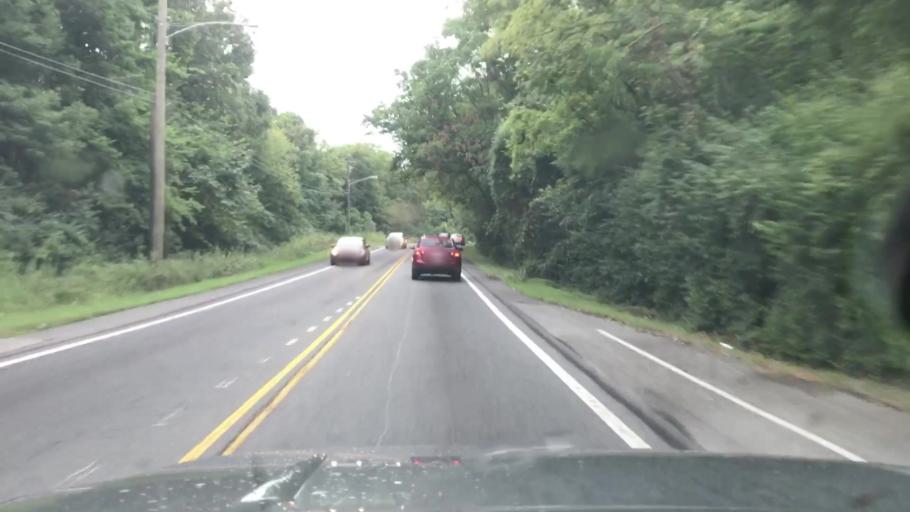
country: US
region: Tennessee
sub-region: Davidson County
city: Lakewood
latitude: 36.1396
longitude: -86.6284
